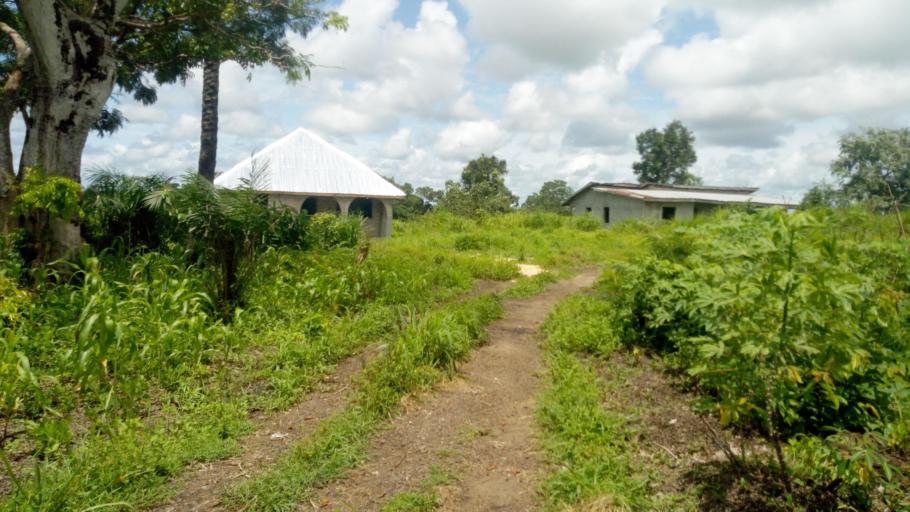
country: SL
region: Northern Province
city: Magburaka
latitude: 8.7112
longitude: -11.9538
